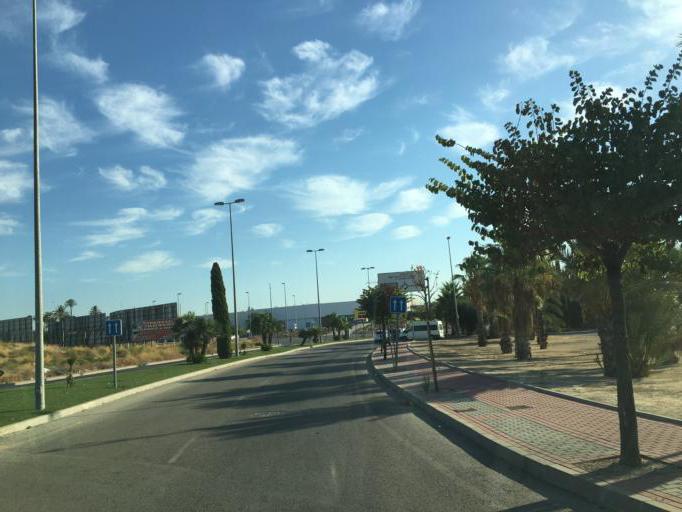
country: ES
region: Murcia
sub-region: Murcia
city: Murcia
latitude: 38.0195
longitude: -1.1408
